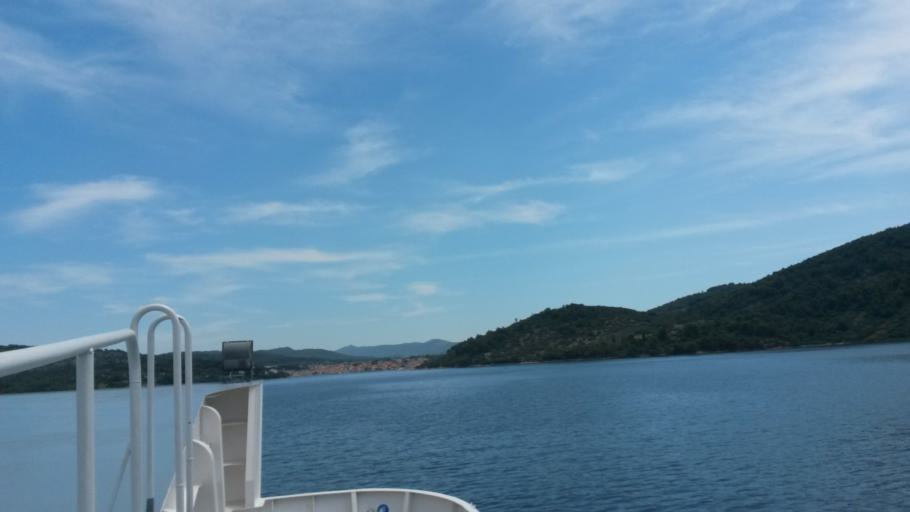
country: HR
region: Dubrovacko-Neretvanska
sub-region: Grad Dubrovnik
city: Vela Luka
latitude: 42.9637
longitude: 16.6861
